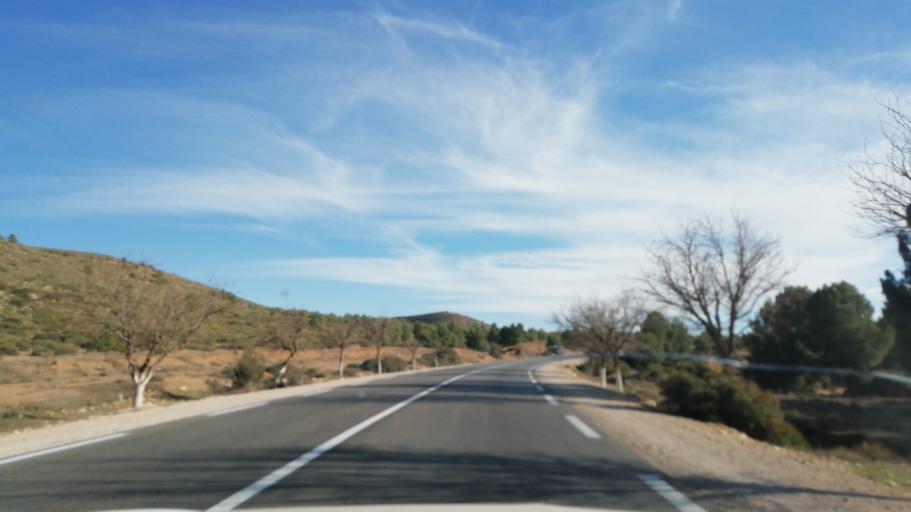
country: DZ
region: Tlemcen
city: Sebdou
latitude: 34.5949
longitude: -1.3207
